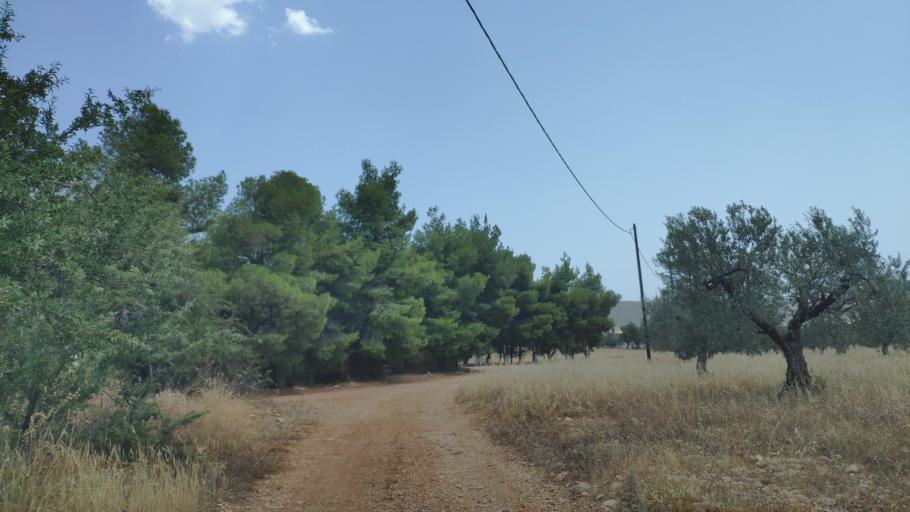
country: GR
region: Peloponnese
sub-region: Nomos Argolidos
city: Didyma
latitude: 37.4699
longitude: 23.1669
